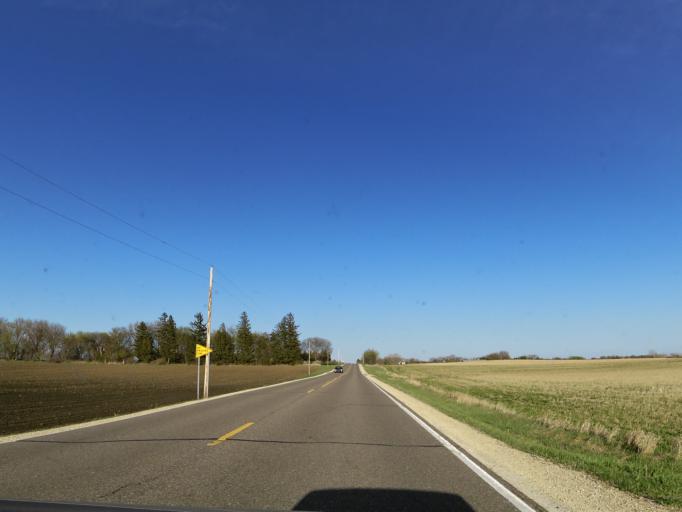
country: US
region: Minnesota
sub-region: Dakota County
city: Farmington
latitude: 44.5435
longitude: -93.0901
